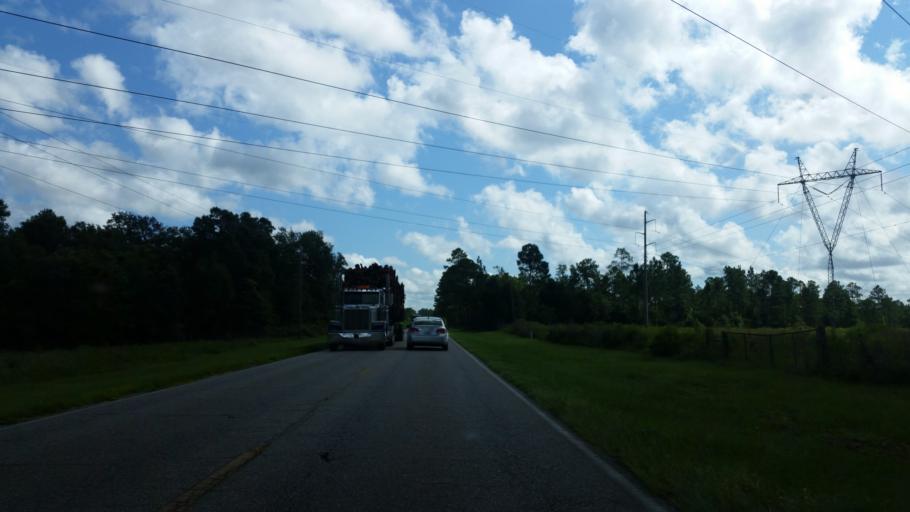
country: US
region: Florida
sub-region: Santa Rosa County
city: Milton
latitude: 30.6687
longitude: -87.0016
